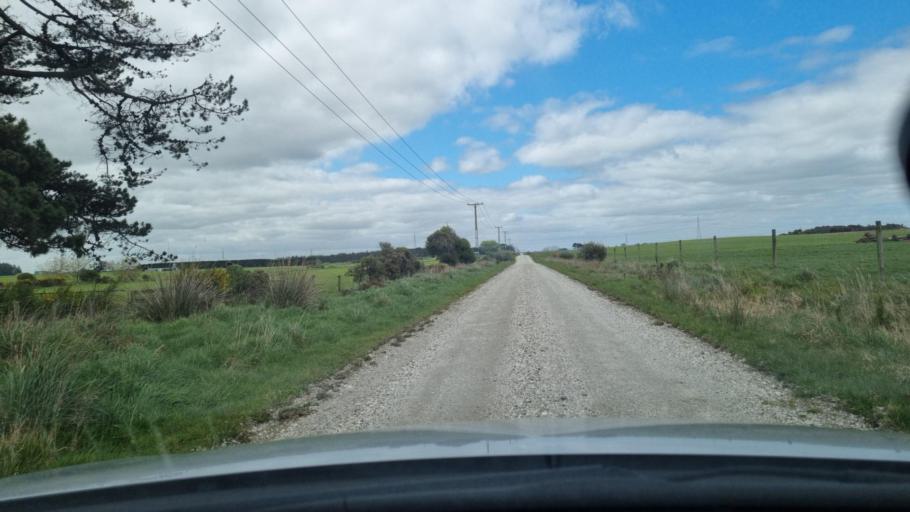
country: NZ
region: Southland
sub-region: Invercargill City
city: Invercargill
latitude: -46.4427
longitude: 168.4280
